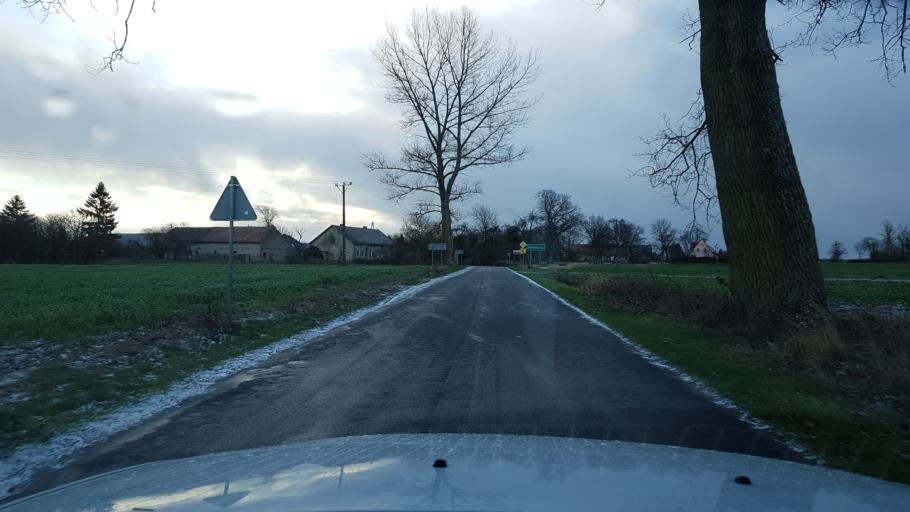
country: PL
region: West Pomeranian Voivodeship
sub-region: Powiat gryficki
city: Brojce
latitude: 54.0360
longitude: 15.3589
